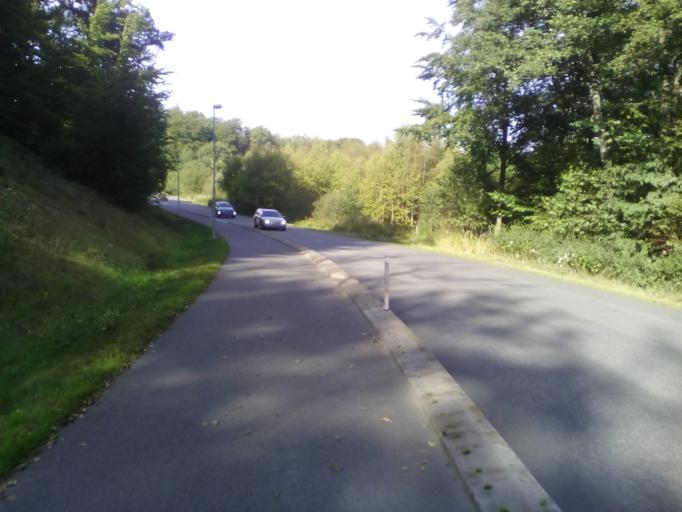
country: SE
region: Blekinge
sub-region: Karlshamns Kommun
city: Karlshamn
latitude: 56.1671
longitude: 14.8966
